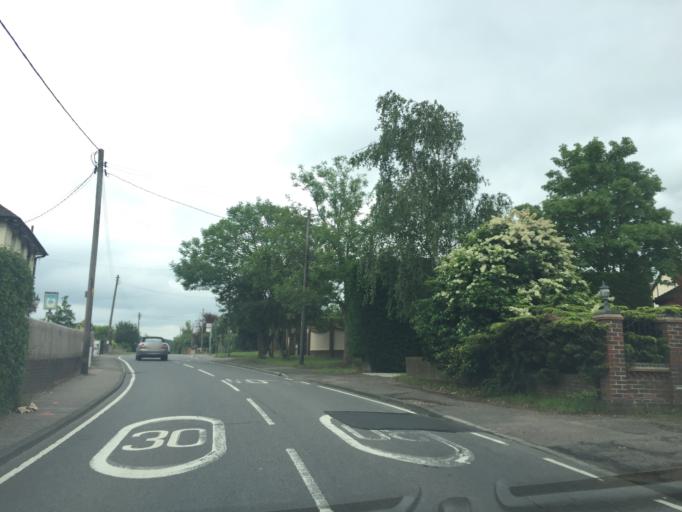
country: GB
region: England
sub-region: Greater London
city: Collier Row
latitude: 51.6283
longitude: 0.1822
